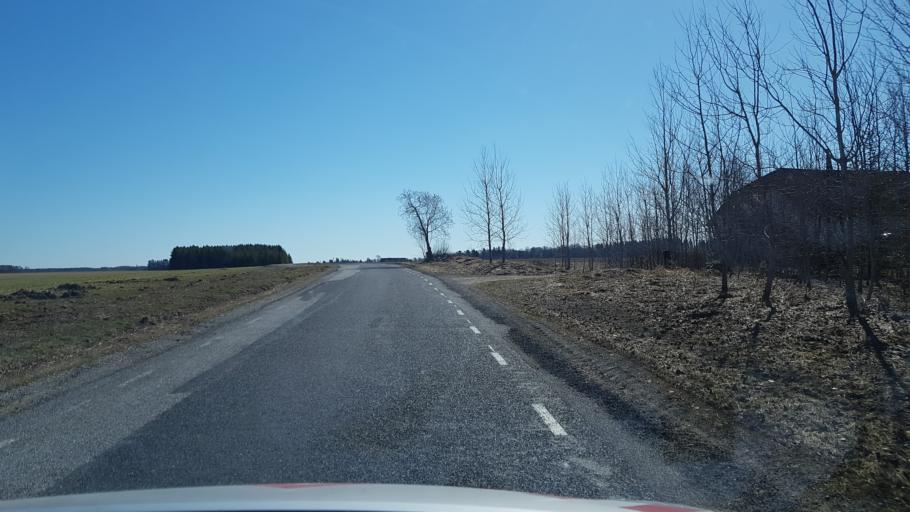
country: EE
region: Laeaene-Virumaa
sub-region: Kadrina vald
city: Kadrina
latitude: 59.4410
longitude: 26.1543
